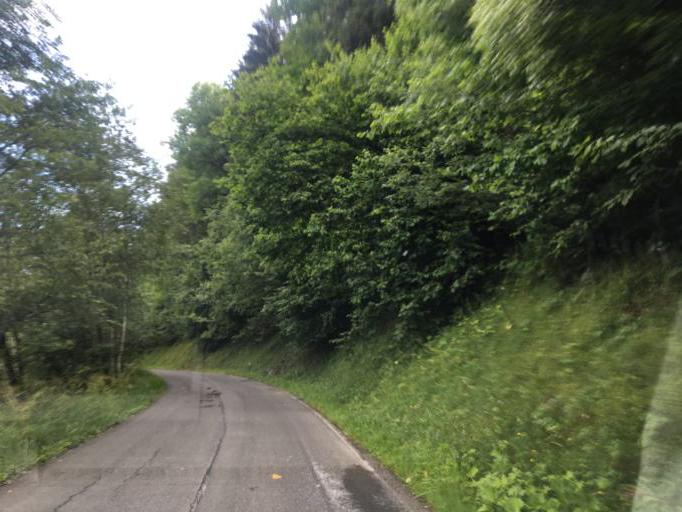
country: AT
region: Styria
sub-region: Politischer Bezirk Liezen
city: Schladming
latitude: 47.3774
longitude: 13.6794
